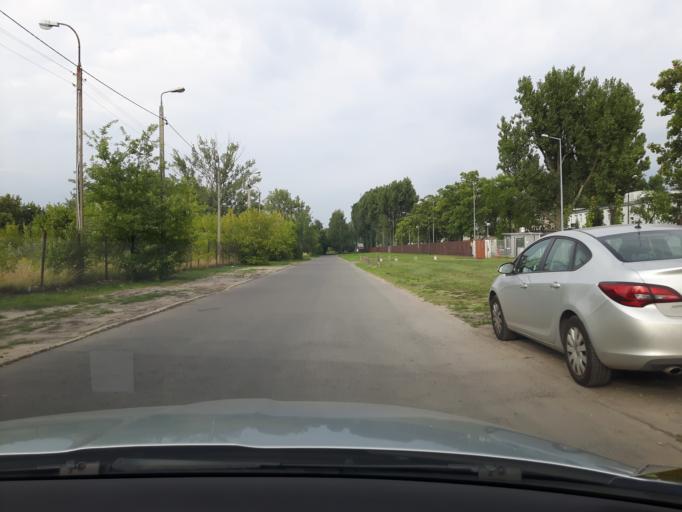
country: PL
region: Masovian Voivodeship
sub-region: Warszawa
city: Praga Poludnie
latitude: 52.2662
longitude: 21.0831
